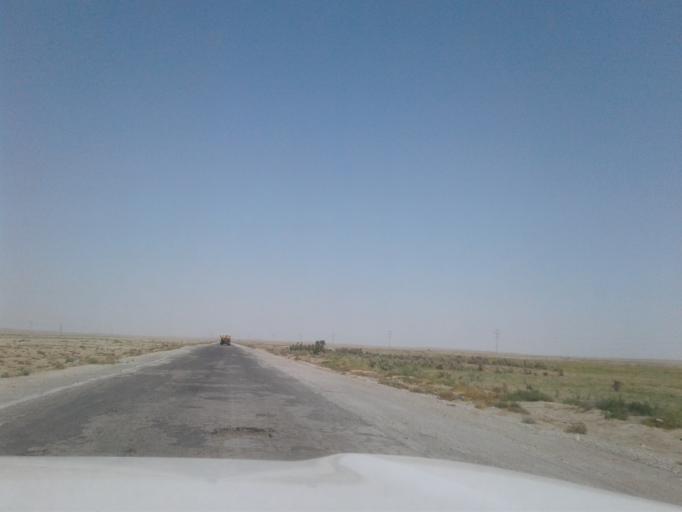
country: TM
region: Balkan
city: Gumdag
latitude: 38.3448
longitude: 54.3644
